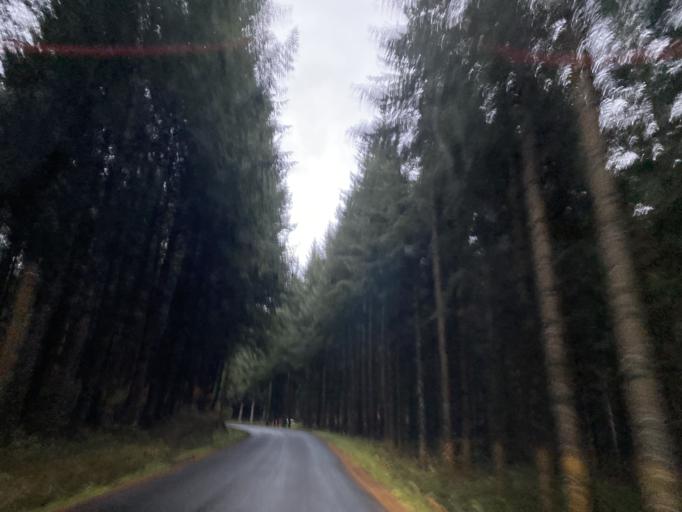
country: FR
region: Auvergne
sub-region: Departement du Puy-de-Dome
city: Cunlhat
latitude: 45.5827
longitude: 3.5625
